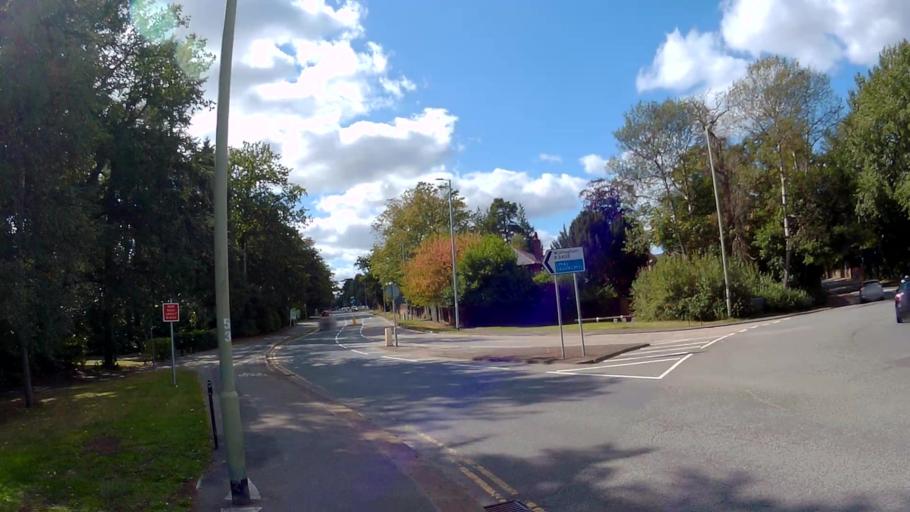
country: GB
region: England
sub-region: Bracknell Forest
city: Binfield
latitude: 51.4213
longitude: -0.7792
